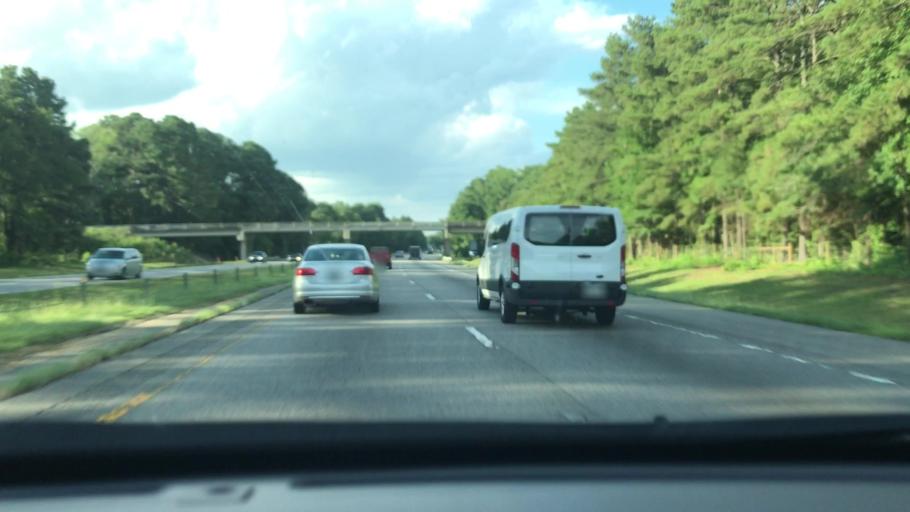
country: US
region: North Carolina
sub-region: Cumberland County
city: Hope Mills
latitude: 34.9070
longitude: -78.9566
